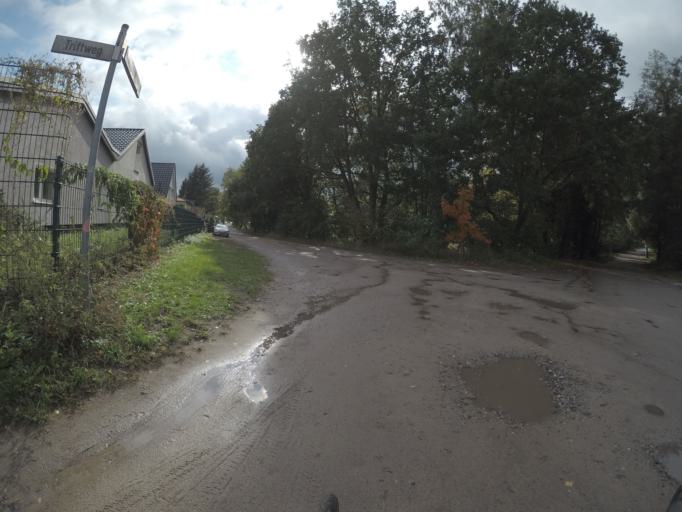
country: DE
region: Berlin
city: Blankenfelde
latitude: 52.6400
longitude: 13.3729
